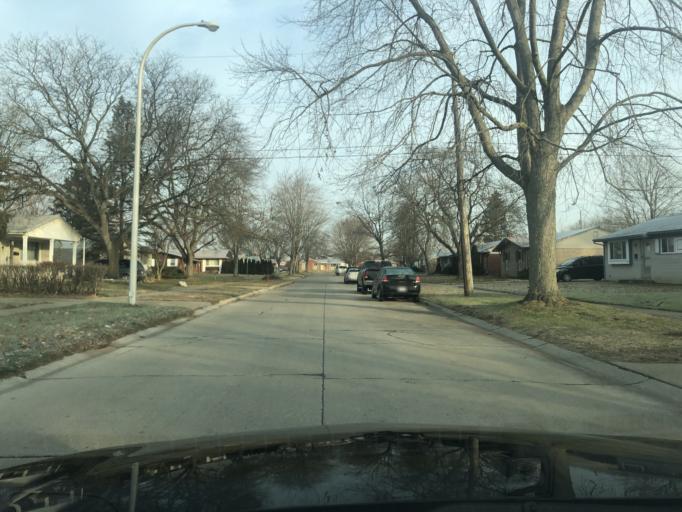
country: US
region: Michigan
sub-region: Wayne County
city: Romulus
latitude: 42.1917
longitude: -83.3330
